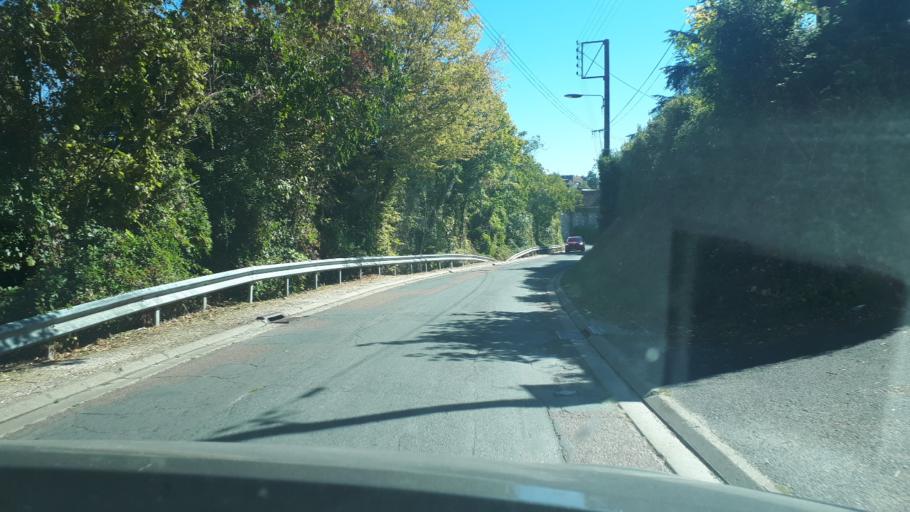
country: FR
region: Centre
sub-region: Departement du Cher
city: Sancerre
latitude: 47.3295
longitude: 2.8304
